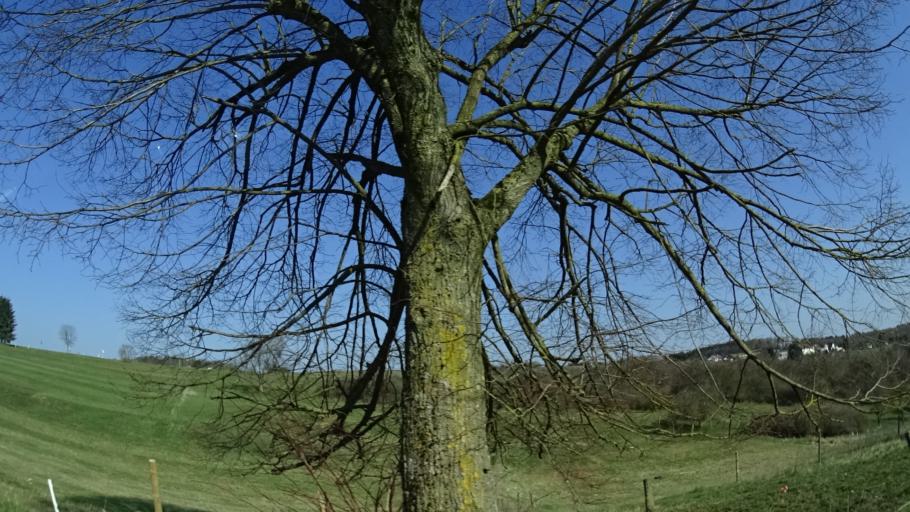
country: DE
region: Rheinland-Pfalz
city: Frauenberg
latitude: 49.6754
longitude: 7.2695
